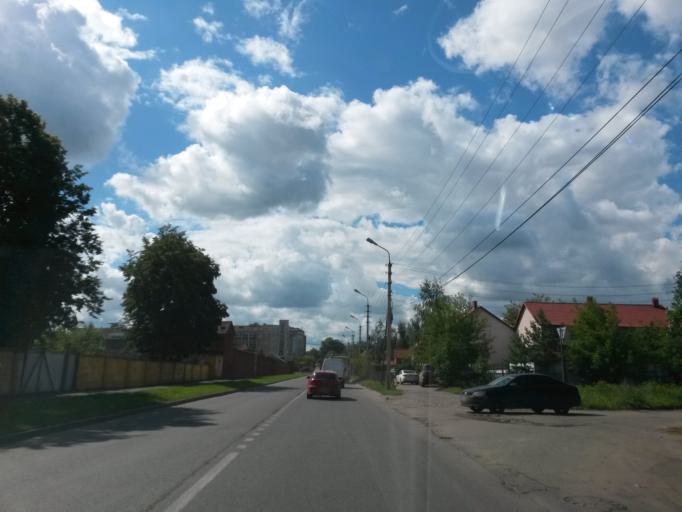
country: RU
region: Jaroslavl
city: Yaroslavl
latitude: 57.6084
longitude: 39.8733
